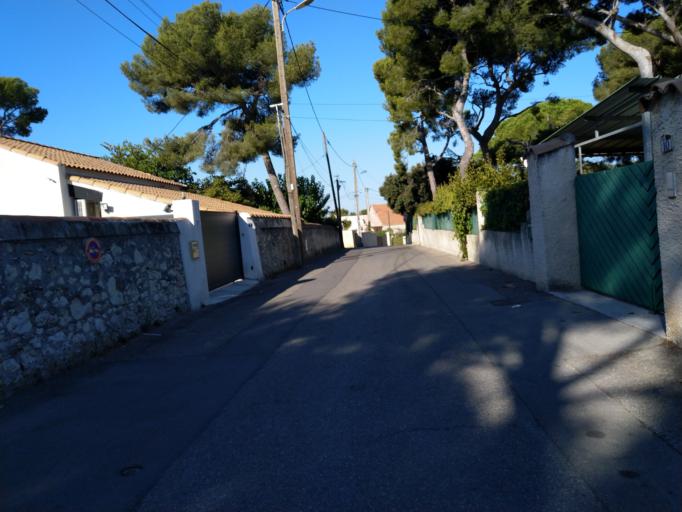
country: FR
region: Provence-Alpes-Cote d'Azur
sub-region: Departement des Bouches-du-Rhone
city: Sausset-les-Pins
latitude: 43.3324
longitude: 5.1193
